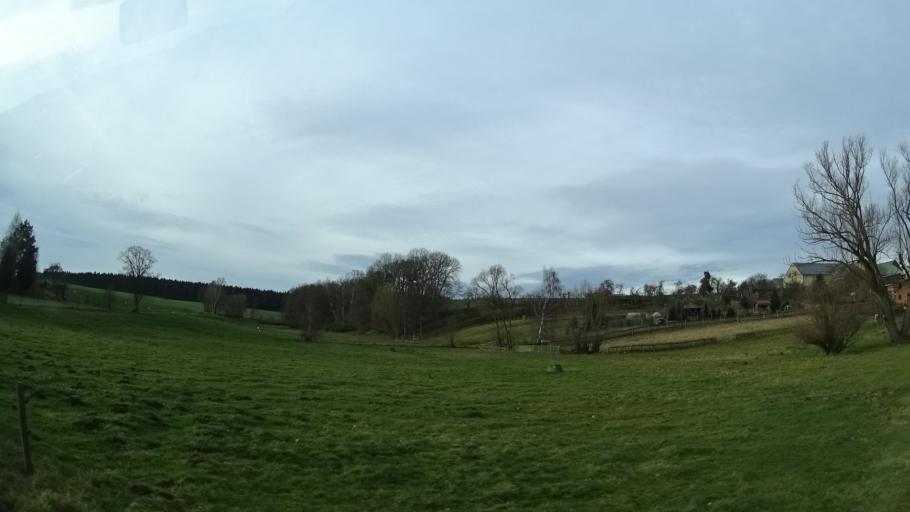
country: DE
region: Thuringia
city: Langenwolschendorf
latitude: 50.6636
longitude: 11.9405
